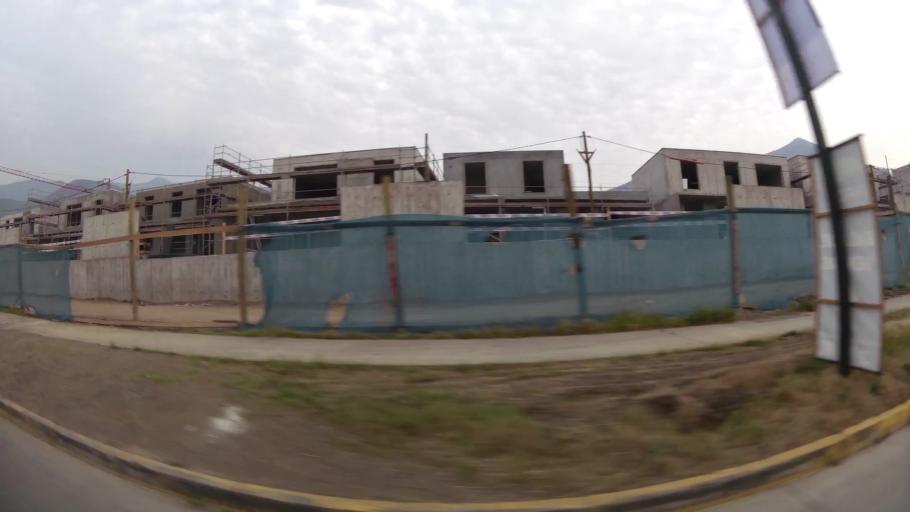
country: CL
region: Santiago Metropolitan
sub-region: Provincia de Chacabuco
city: Chicureo Abajo
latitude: -33.3240
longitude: -70.6334
